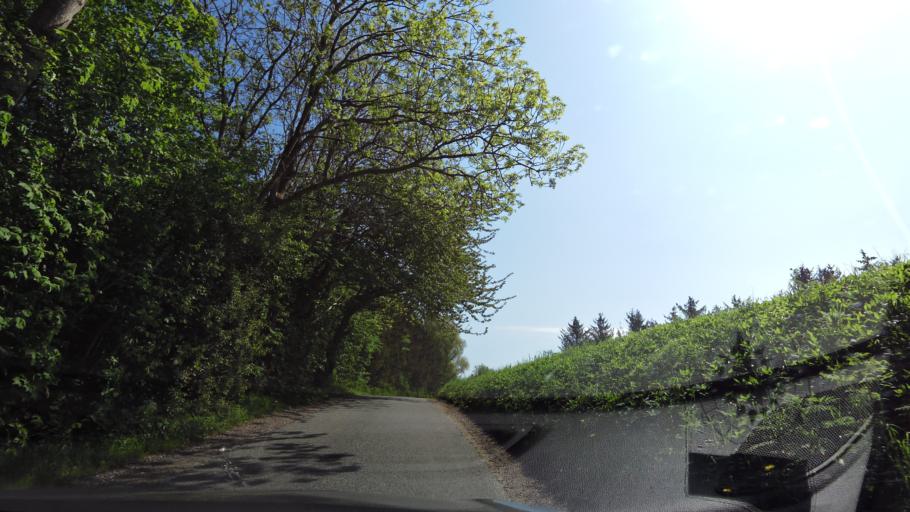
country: DK
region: South Denmark
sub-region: Nyborg Kommune
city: Ullerslev
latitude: 55.2733
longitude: 10.6846
